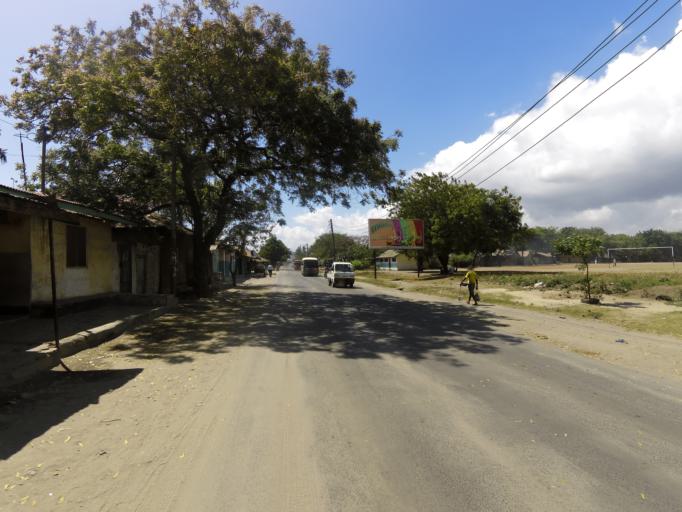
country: TZ
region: Dar es Salaam
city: Magomeni
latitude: -6.8015
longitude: 39.2566
